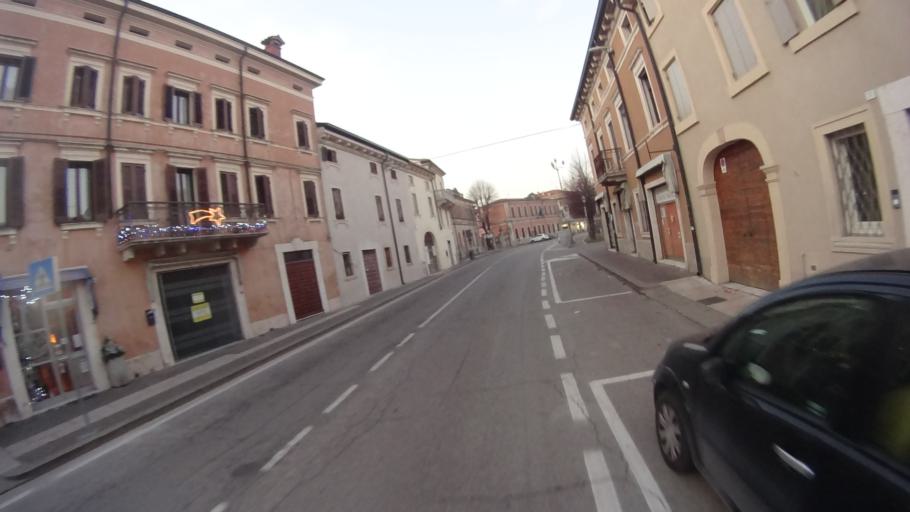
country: IT
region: Veneto
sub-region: Provincia di Verona
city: Povegliano Veronese
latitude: 45.3464
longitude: 10.8812
